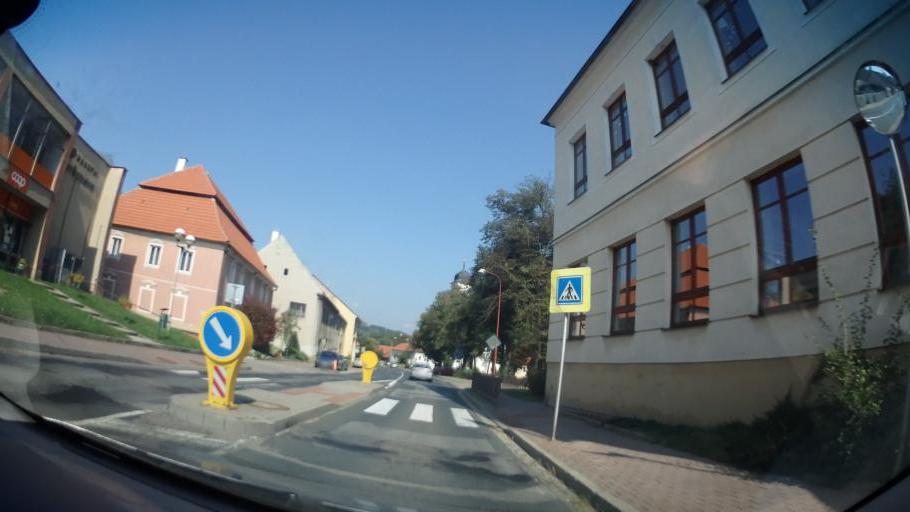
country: CZ
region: South Moravian
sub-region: Okres Brno-Venkov
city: Nedvedice
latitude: 49.4237
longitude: 16.3523
